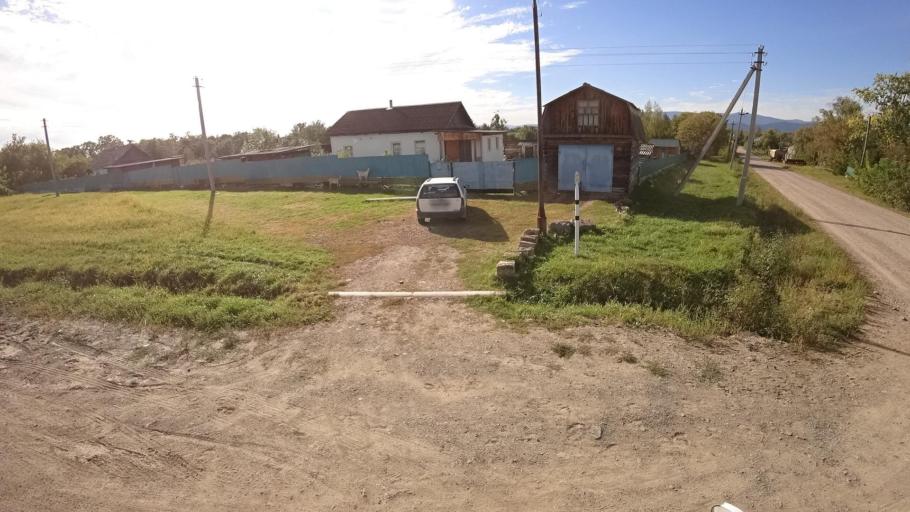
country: RU
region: Primorskiy
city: Dostoyevka
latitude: 44.3039
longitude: 133.4556
